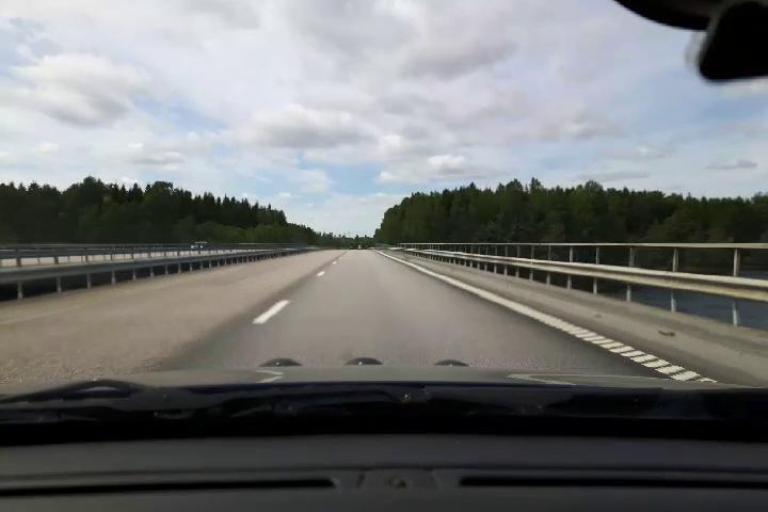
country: SE
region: Uppsala
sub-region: Alvkarleby Kommun
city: AElvkarleby
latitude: 60.4710
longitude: 17.3958
